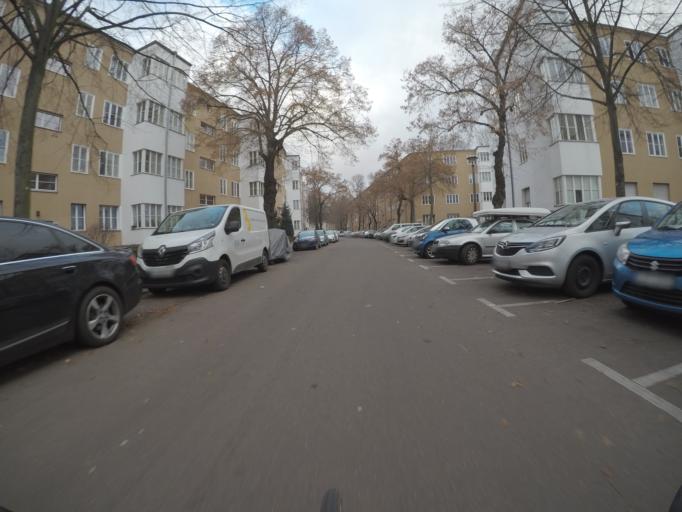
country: DE
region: Berlin
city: Niederschoneweide
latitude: 52.4556
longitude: 13.5194
